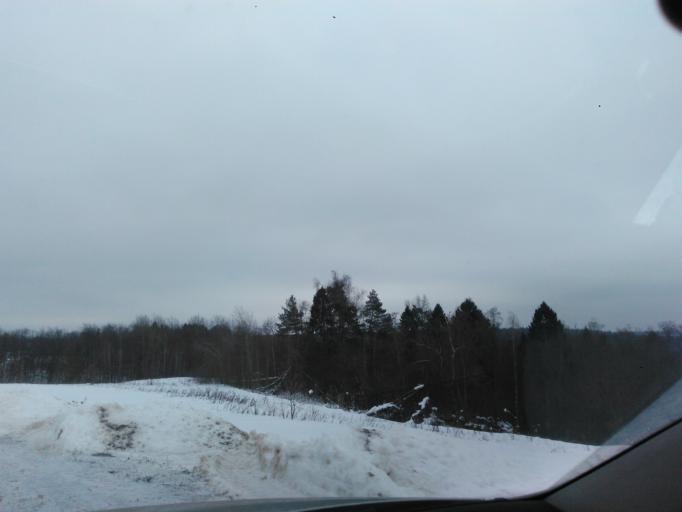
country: RU
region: Moskovskaya
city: Podosinki
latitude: 56.2754
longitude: 37.6001
